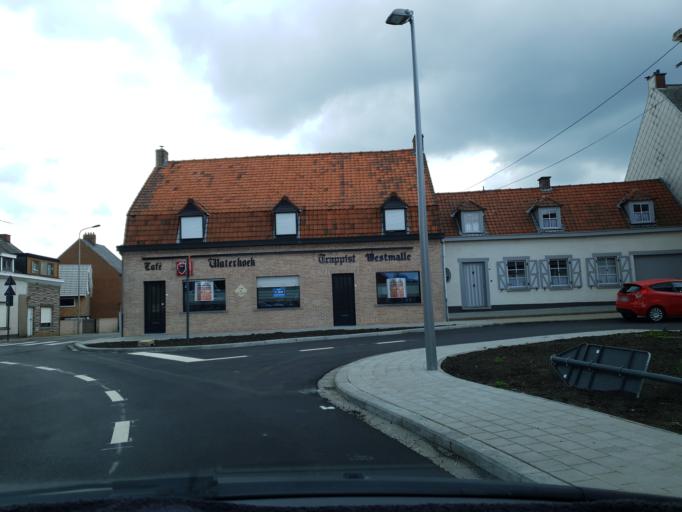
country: BE
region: Flanders
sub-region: Provincie West-Vlaanderen
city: Avelgem
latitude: 50.7798
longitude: 3.4650
